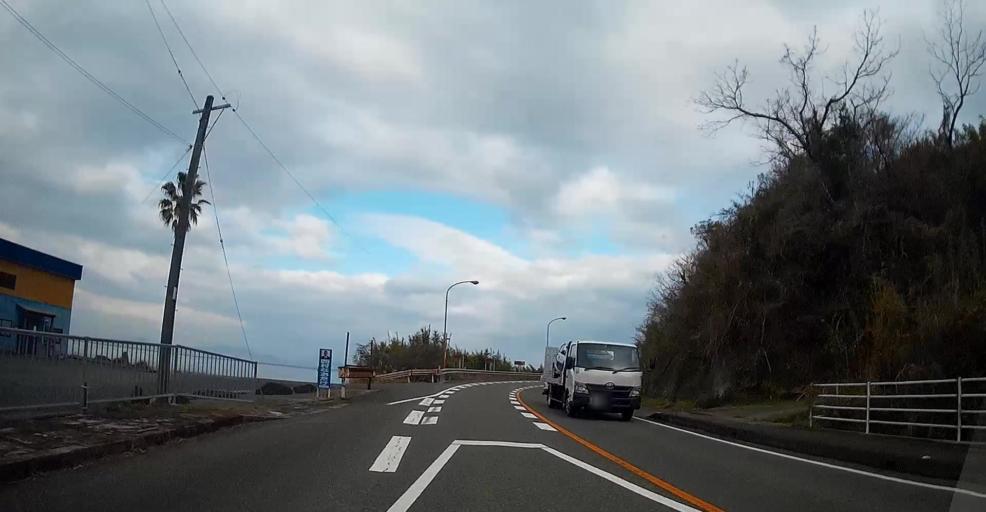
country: JP
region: Kumamoto
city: Hondo
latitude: 32.5004
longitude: 130.2985
